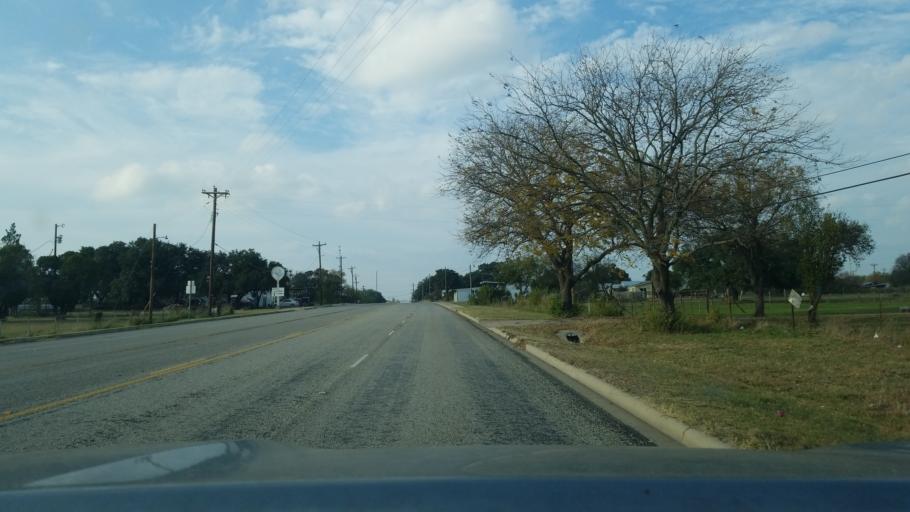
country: US
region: Texas
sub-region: Lampasas County
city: Lampasas
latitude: 31.2105
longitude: -98.3902
